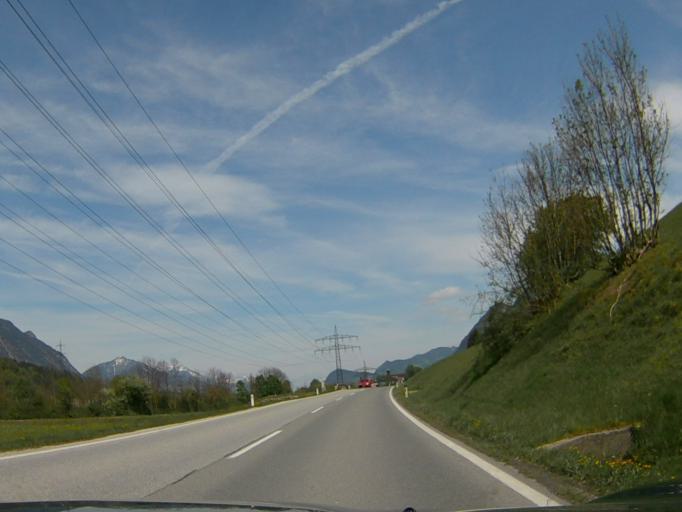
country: AT
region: Tyrol
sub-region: Politischer Bezirk Schwaz
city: Jenbach
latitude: 47.3868
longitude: 11.7870
